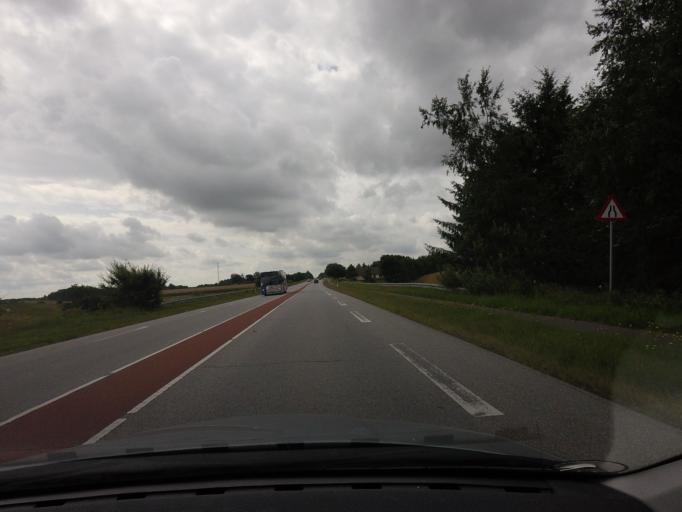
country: DK
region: North Denmark
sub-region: Hjorring Kommune
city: Hjorring
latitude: 57.4061
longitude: 9.9886
